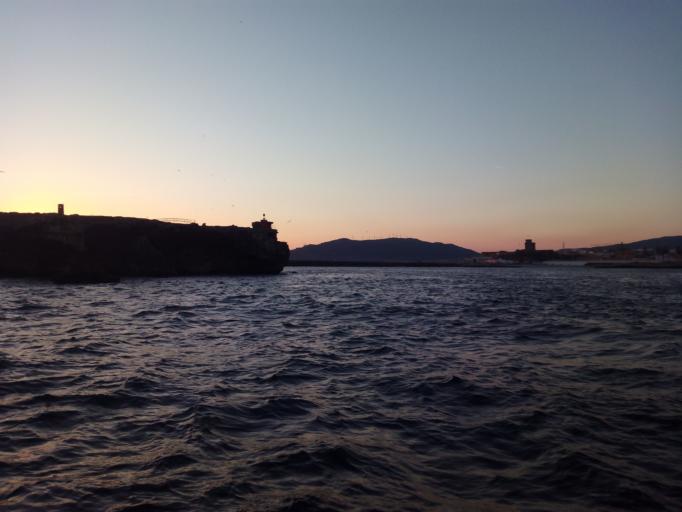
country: ES
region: Andalusia
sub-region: Provincia de Cadiz
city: Tarifa
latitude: 36.0034
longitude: -5.6054
